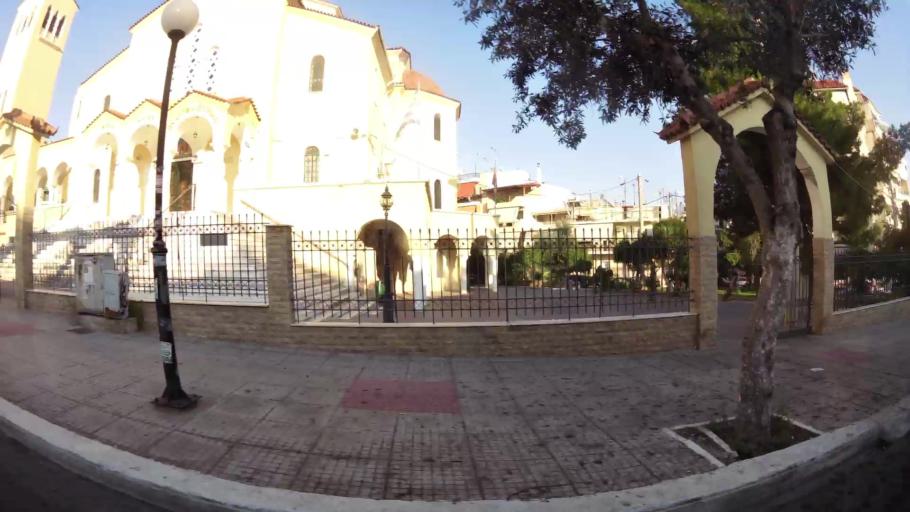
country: GR
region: Attica
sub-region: Nomos Piraios
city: Korydallos
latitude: 37.9774
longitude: 23.6409
